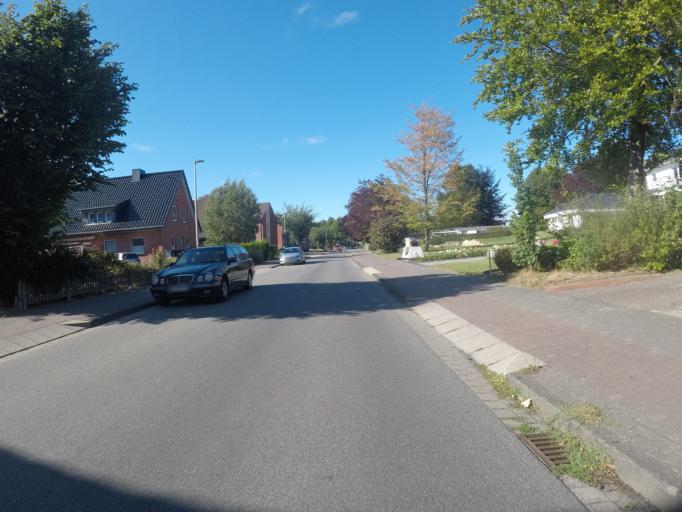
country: DE
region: Lower Saxony
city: Otterndorf
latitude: 53.8103
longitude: 8.9067
